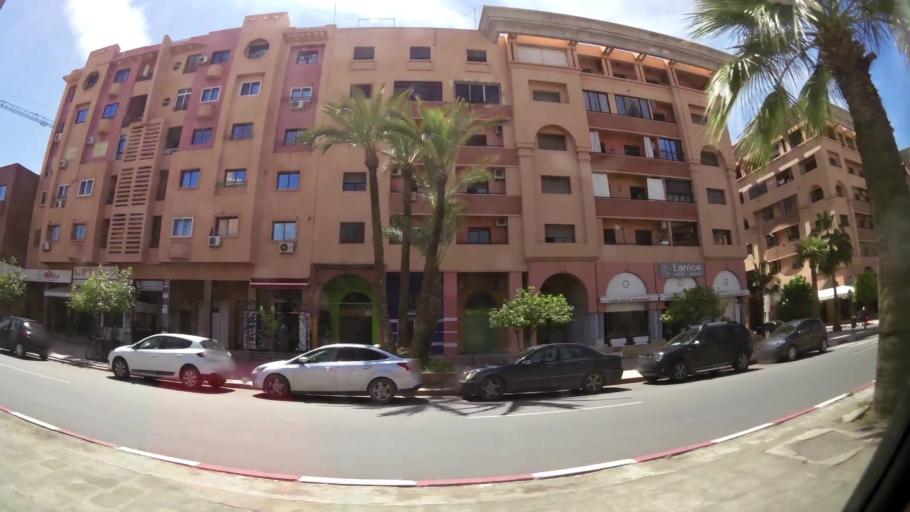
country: MA
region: Marrakech-Tensift-Al Haouz
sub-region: Marrakech
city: Marrakesh
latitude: 31.6573
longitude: -8.0047
